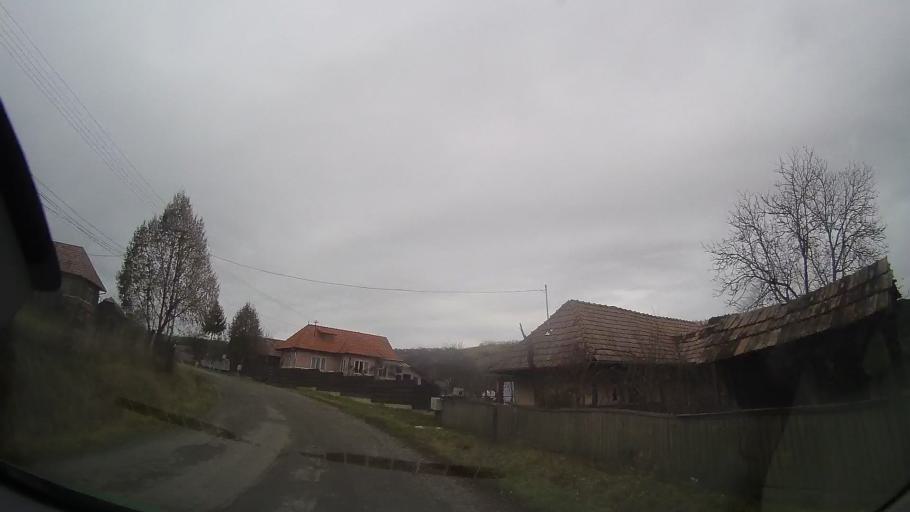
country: RO
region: Mures
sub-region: Comuna Bala
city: Bala
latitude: 46.7119
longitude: 24.5020
